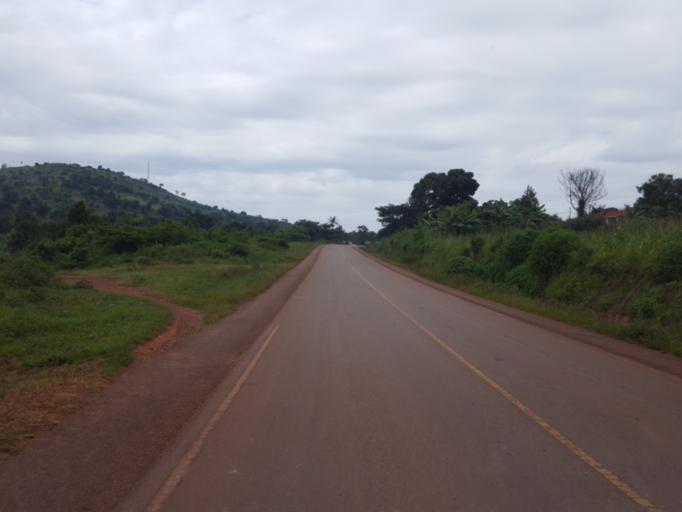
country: UG
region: Central Region
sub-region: Mityana District
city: Mityana
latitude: 0.6551
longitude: 32.0938
